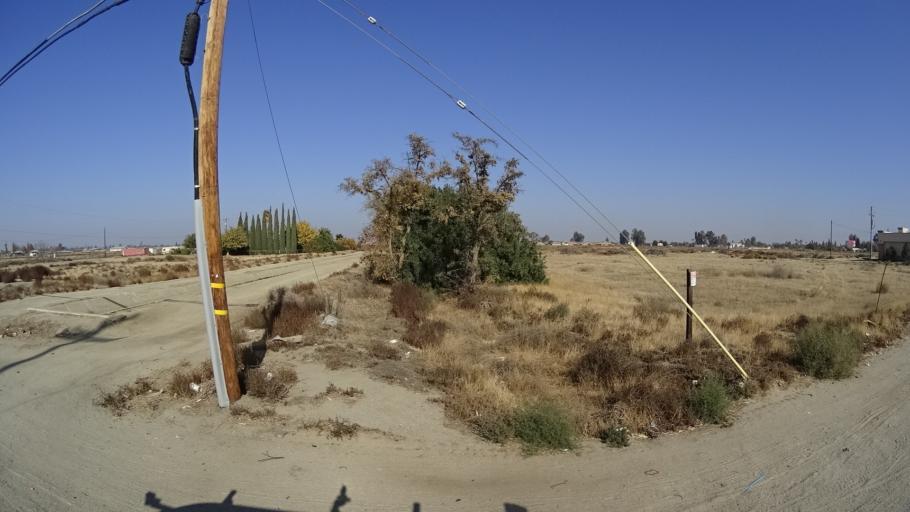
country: US
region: California
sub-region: Kern County
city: Greenfield
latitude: 35.2667
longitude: -119.0277
